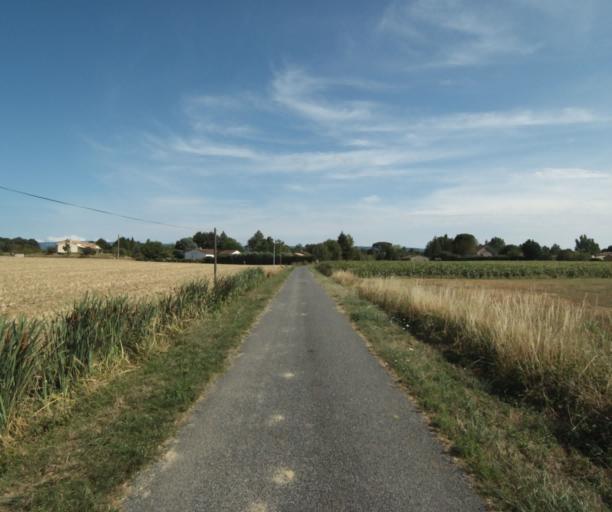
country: FR
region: Midi-Pyrenees
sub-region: Departement de la Haute-Garonne
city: Revel
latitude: 43.5010
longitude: 1.9701
